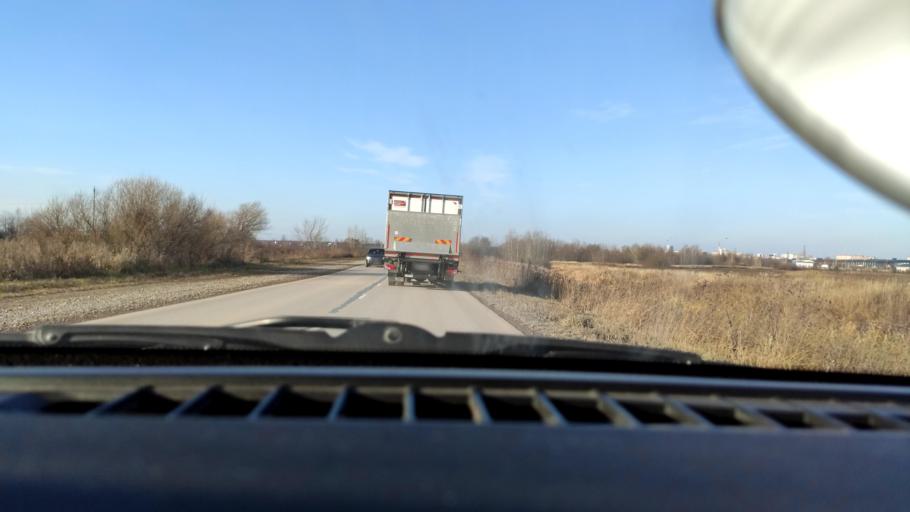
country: RU
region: Perm
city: Kondratovo
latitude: 58.0032
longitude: 56.0628
